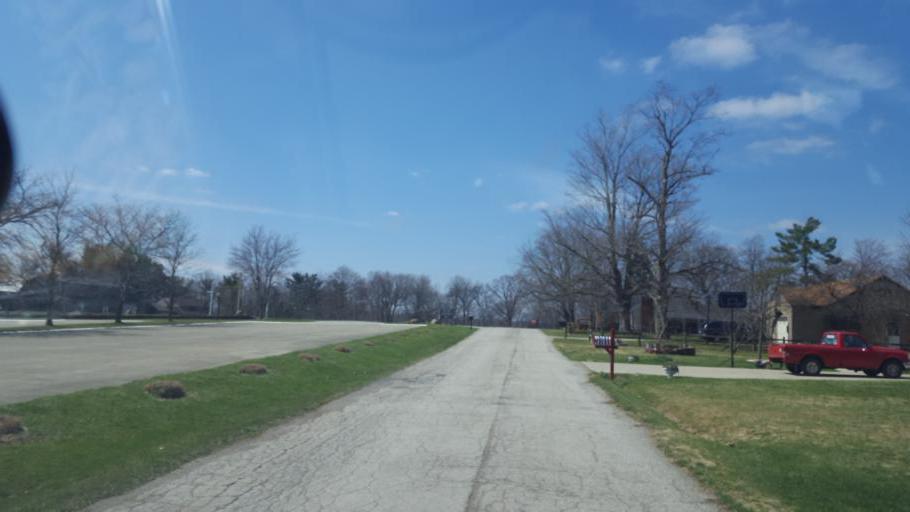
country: US
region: Ohio
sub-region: Richland County
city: Lincoln Heights
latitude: 40.7872
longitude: -82.4953
